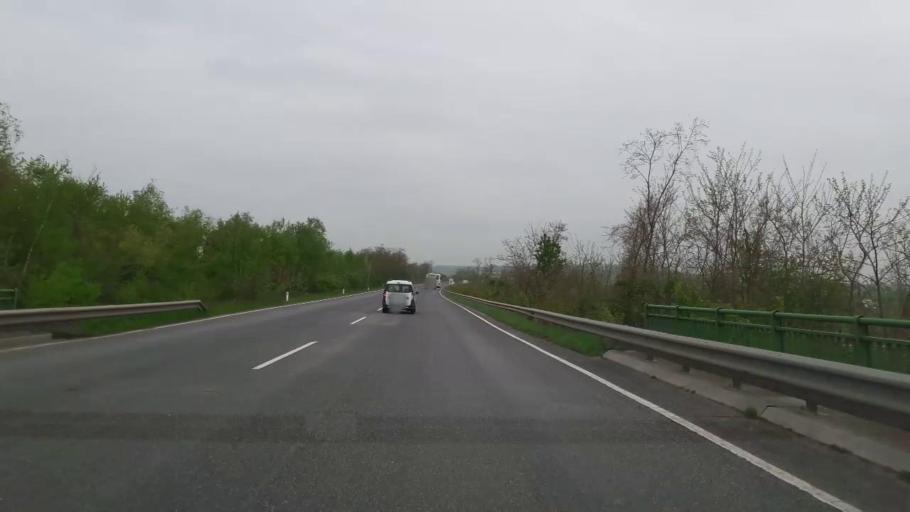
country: AT
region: Lower Austria
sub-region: Politischer Bezirk Hollabrunn
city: Hollabrunn
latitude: 48.5500
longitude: 16.0725
